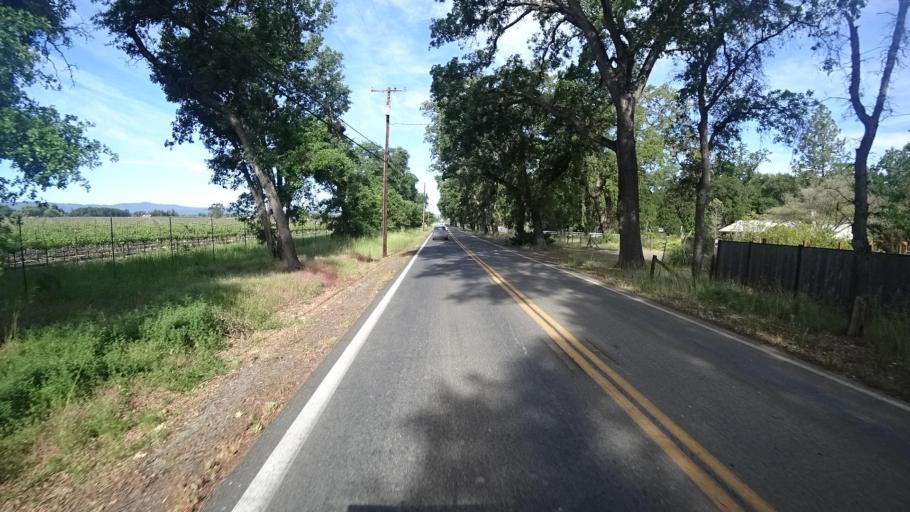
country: US
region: California
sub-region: Lake County
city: Soda Bay
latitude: 39.0076
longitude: -122.8206
